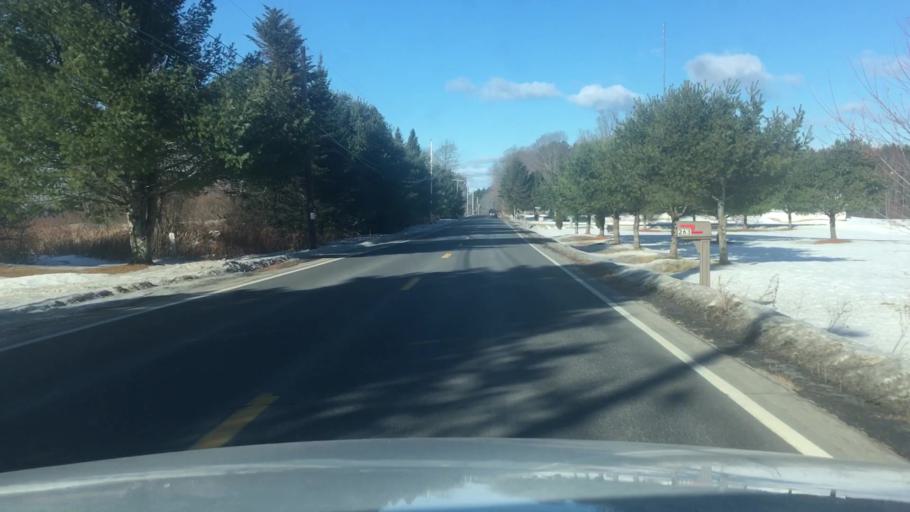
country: US
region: Maine
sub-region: Somerset County
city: Skowhegan
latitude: 44.7411
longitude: -69.6883
